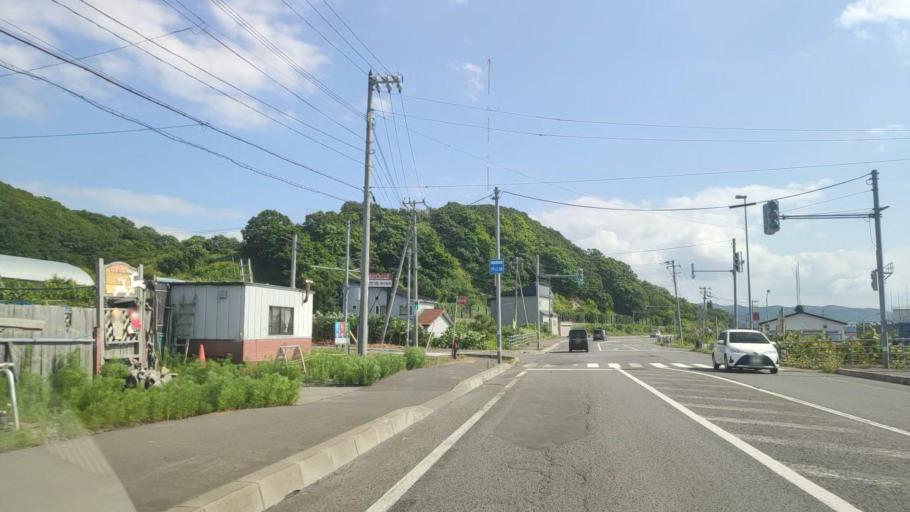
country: JP
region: Hokkaido
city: Rumoi
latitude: 43.9588
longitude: 141.6439
